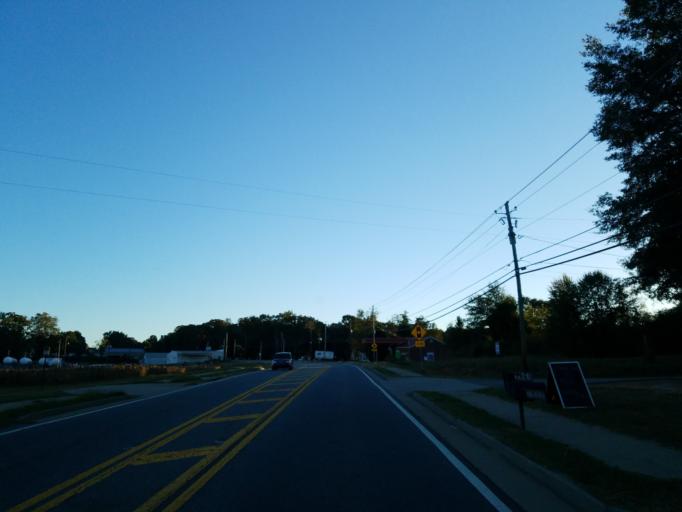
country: US
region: Georgia
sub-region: Forsyth County
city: Cumming
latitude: 34.2629
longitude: -84.1049
